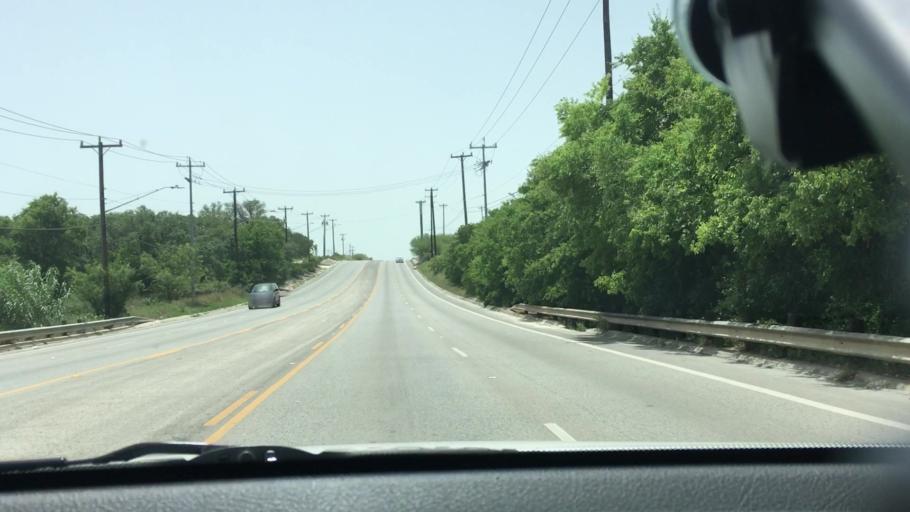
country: US
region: Texas
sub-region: Bexar County
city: Live Oak
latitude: 29.5594
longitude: -98.3509
